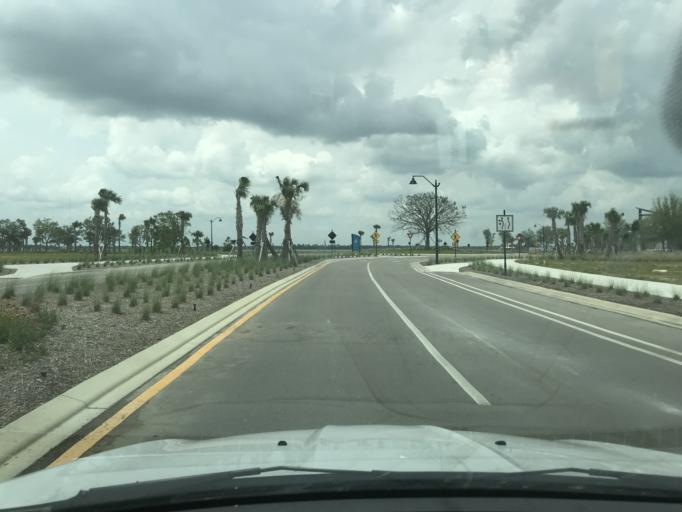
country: US
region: Florida
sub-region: Lee County
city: Olga
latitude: 26.7813
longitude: -81.7413
